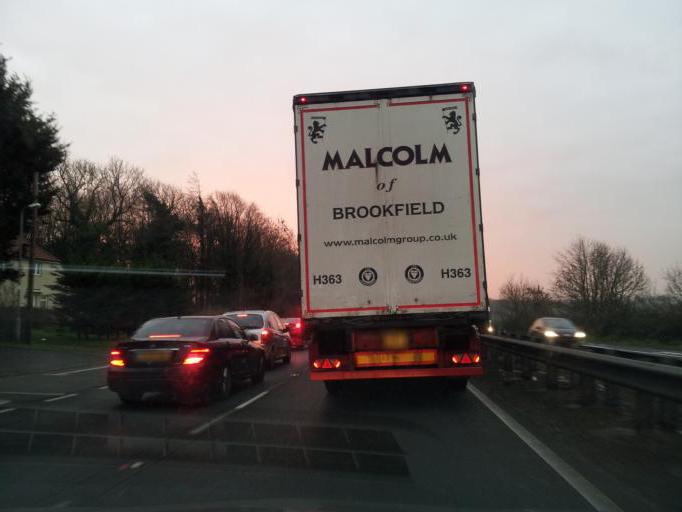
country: GB
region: England
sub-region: Peterborough
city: Thornhaugh
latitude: 52.5922
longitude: -0.4177
